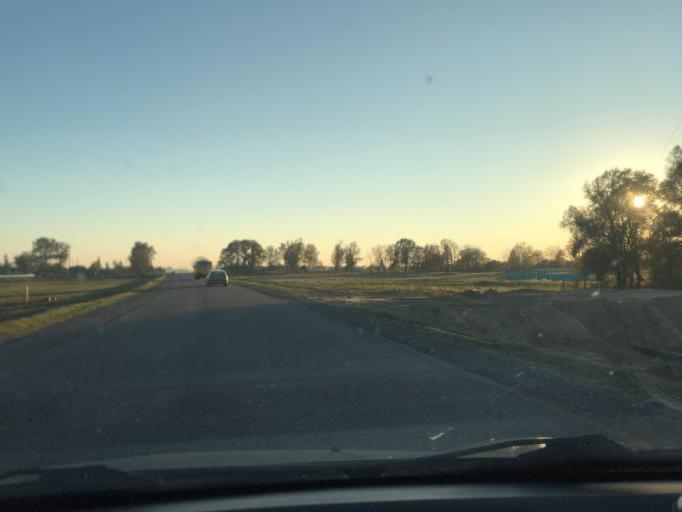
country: BY
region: Gomel
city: Brahin
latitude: 51.7979
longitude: 30.2636
